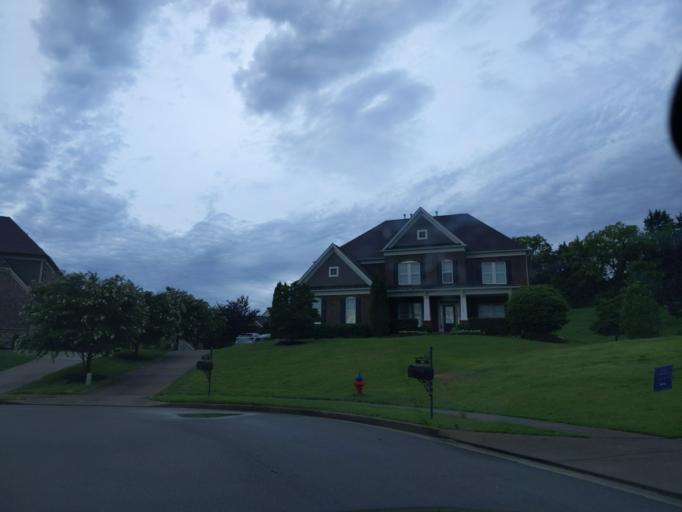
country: US
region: Tennessee
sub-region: Williamson County
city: Brentwood Estates
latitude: 36.0116
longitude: -86.7468
